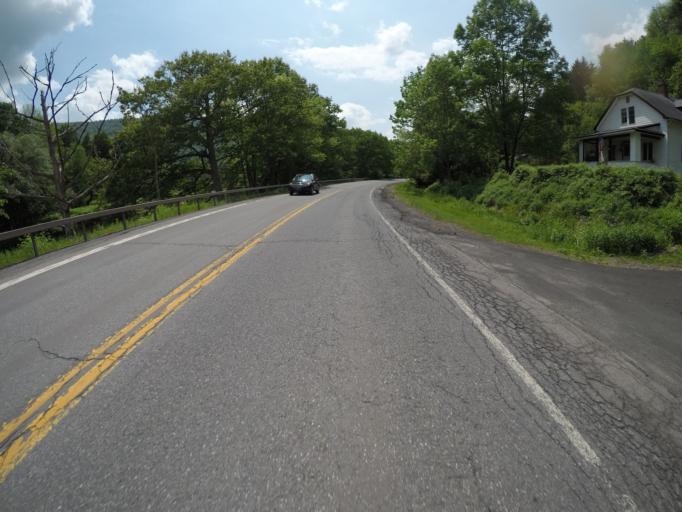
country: US
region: New York
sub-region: Delaware County
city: Stamford
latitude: 42.1513
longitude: -74.6310
